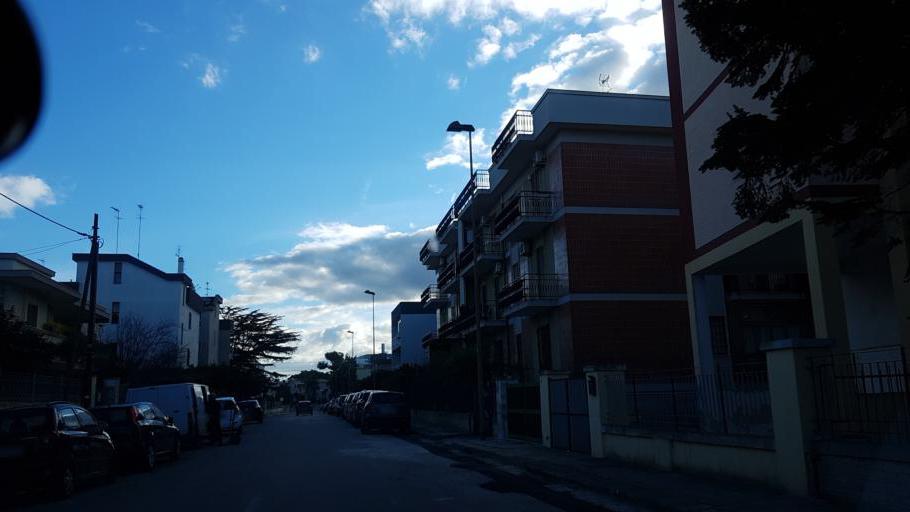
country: IT
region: Apulia
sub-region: Provincia di Brindisi
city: Brindisi
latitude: 40.6493
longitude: 17.9414
